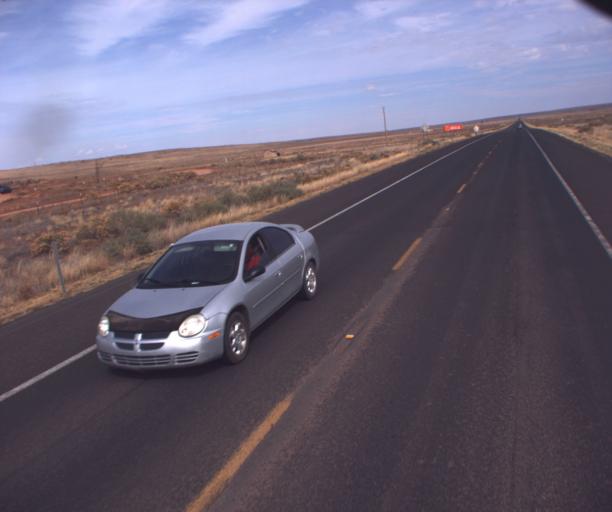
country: US
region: Arizona
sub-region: Apache County
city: Ganado
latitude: 35.7641
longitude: -109.6243
